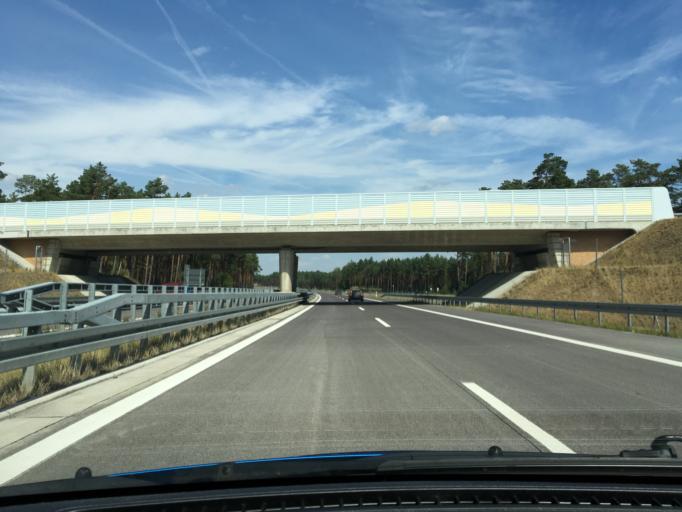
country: DE
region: Mecklenburg-Vorpommern
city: Gross Laasch
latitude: 53.3937
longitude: 11.5320
